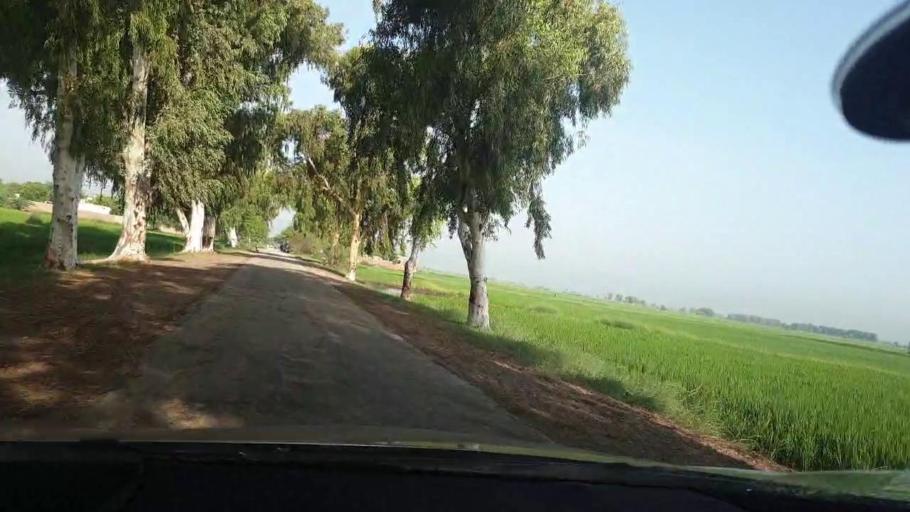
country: PK
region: Sindh
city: Kambar
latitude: 27.6527
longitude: 68.0361
